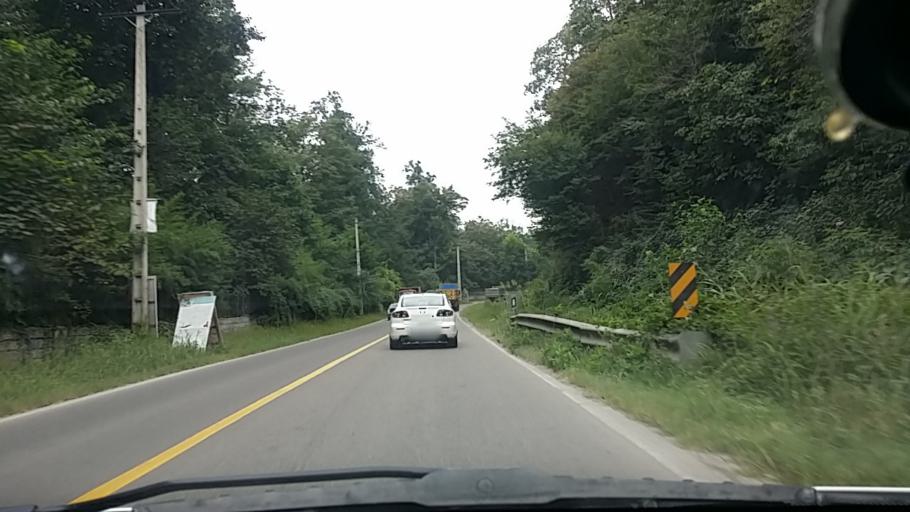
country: IR
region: Mazandaran
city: Chalus
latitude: 36.6074
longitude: 51.3865
